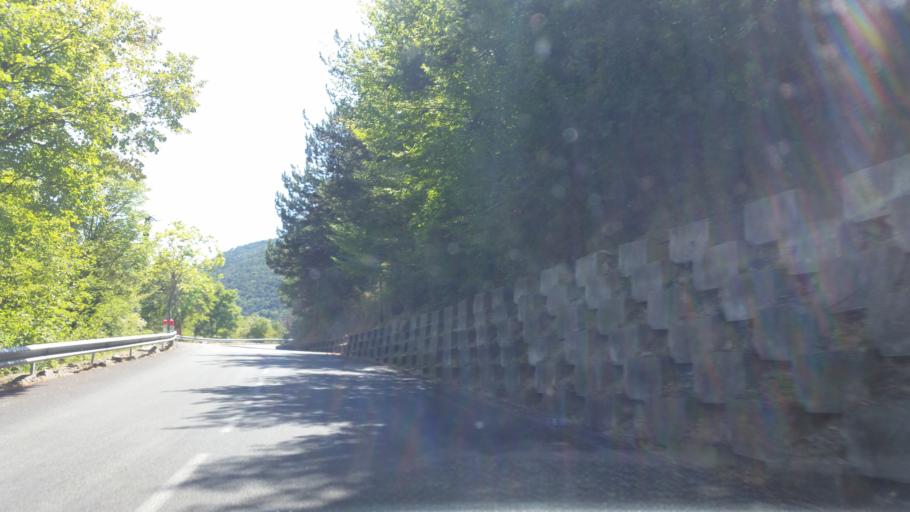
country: FR
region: Provence-Alpes-Cote d'Azur
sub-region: Departement des Alpes-Maritimes
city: Breil-sur-Roya
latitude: 43.9379
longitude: 7.4785
